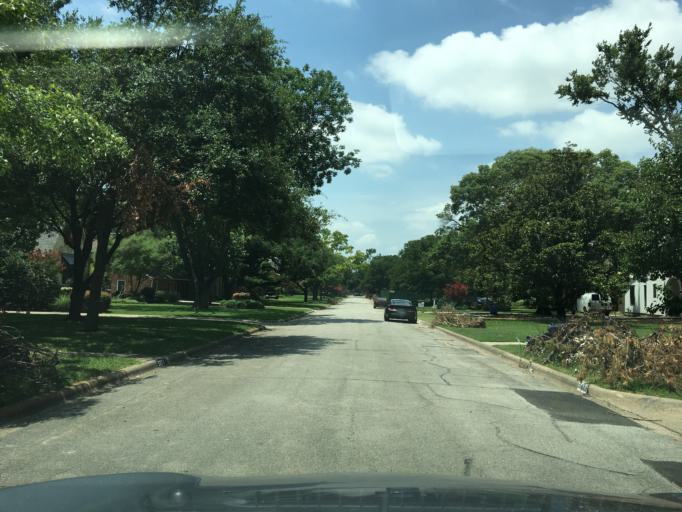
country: US
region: Texas
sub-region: Dallas County
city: Addison
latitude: 32.9176
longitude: -96.8079
